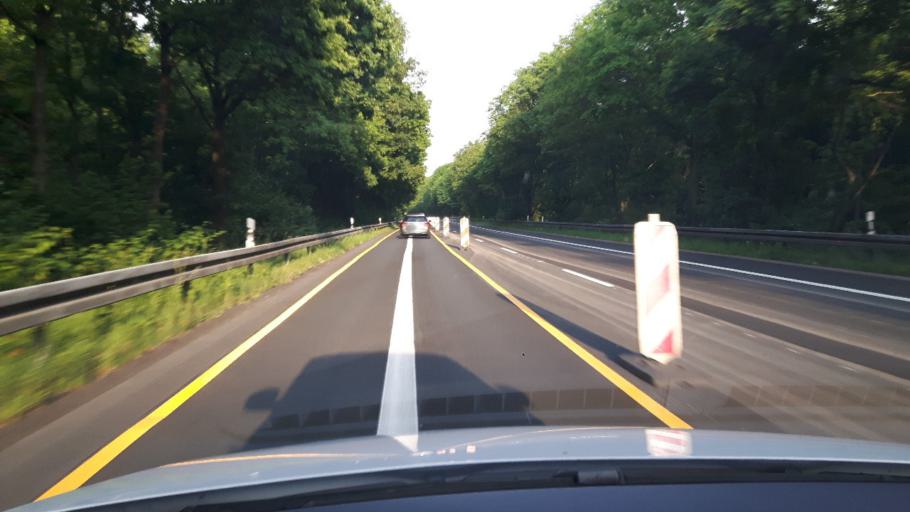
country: DE
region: North Rhine-Westphalia
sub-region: Regierungsbezirk Koln
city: Siegburg
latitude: 50.8140
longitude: 7.2154
